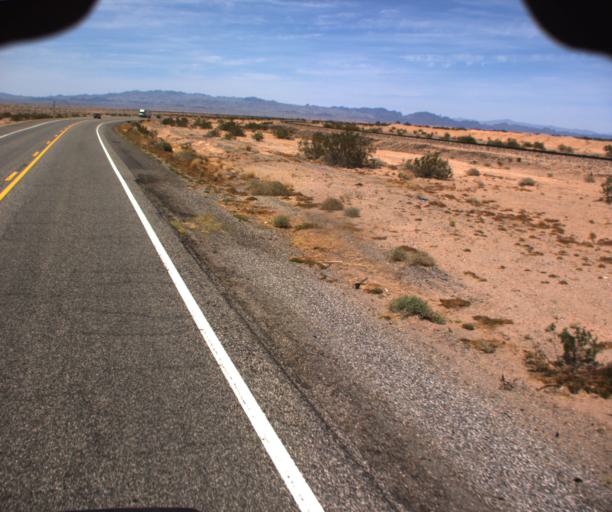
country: US
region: Arizona
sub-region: La Paz County
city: Parker
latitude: 34.0292
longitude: -114.2566
